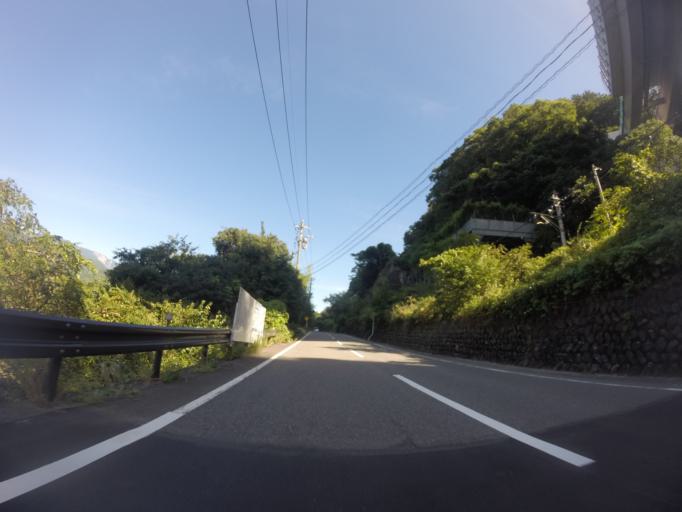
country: JP
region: Shizuoka
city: Fujinomiya
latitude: 35.3154
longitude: 138.4547
